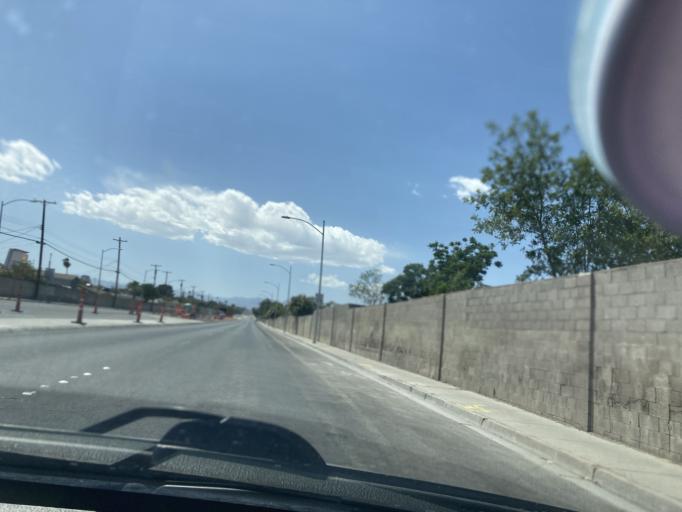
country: US
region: Nevada
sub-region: Clark County
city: North Las Vegas
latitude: 36.1813
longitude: -115.1165
